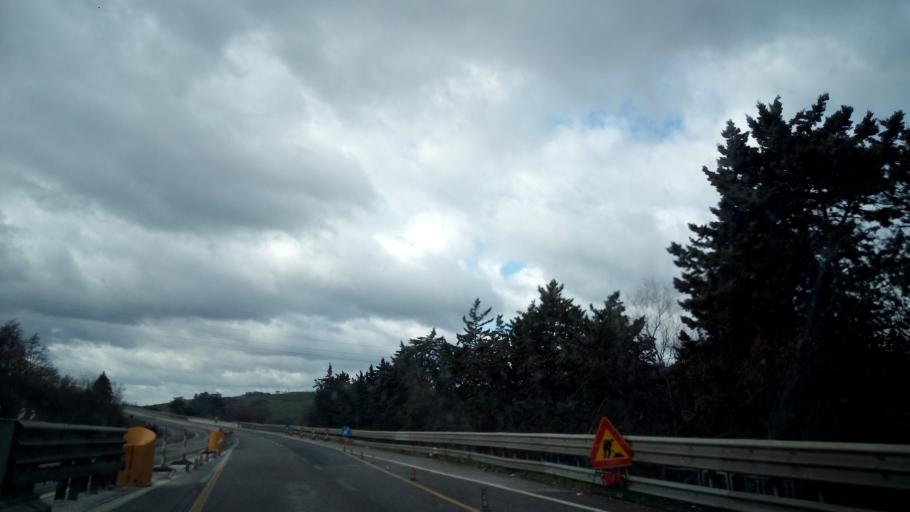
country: IT
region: Campania
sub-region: Provincia di Avellino
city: Flumeri
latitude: 41.0911
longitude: 15.1505
